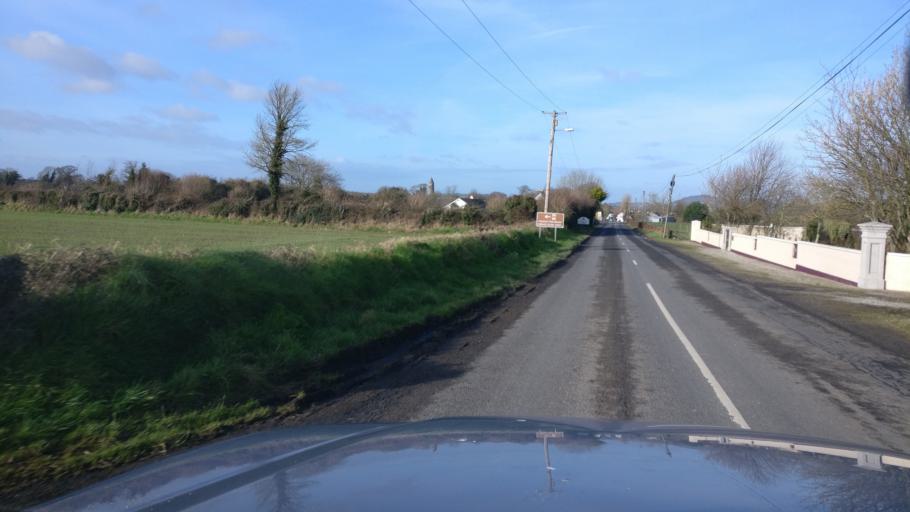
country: IE
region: Leinster
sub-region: Laois
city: Stradbally
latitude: 52.9562
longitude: -7.1990
